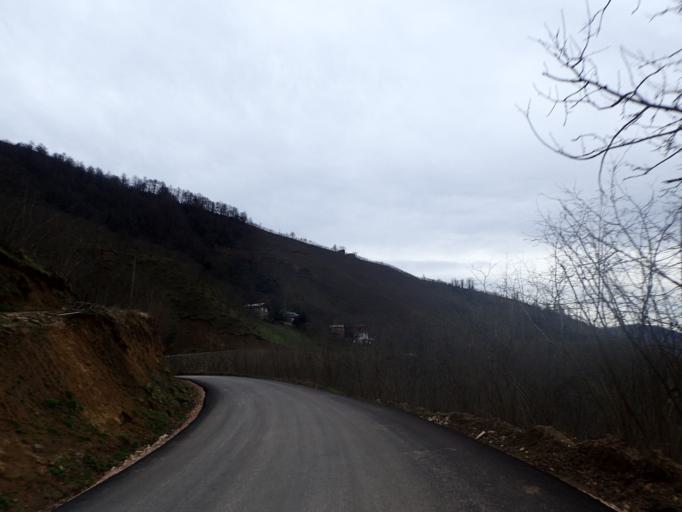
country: TR
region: Ordu
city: Camas
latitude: 40.8851
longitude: 37.5219
